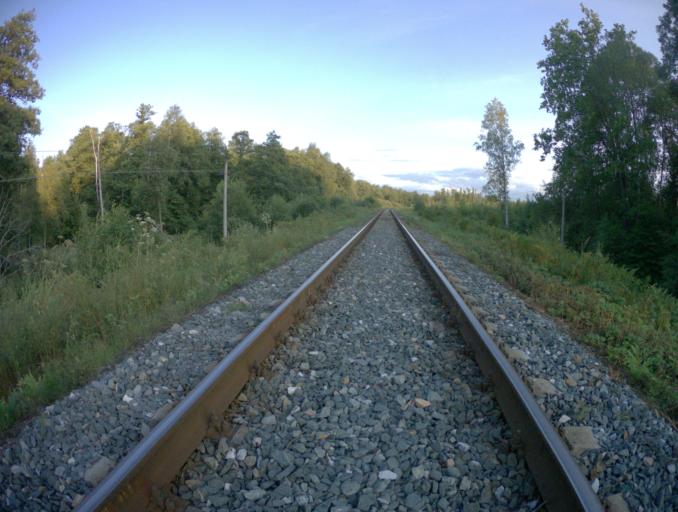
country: RU
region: Vladimir
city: Raduzhnyy
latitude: 56.0422
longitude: 40.3845
